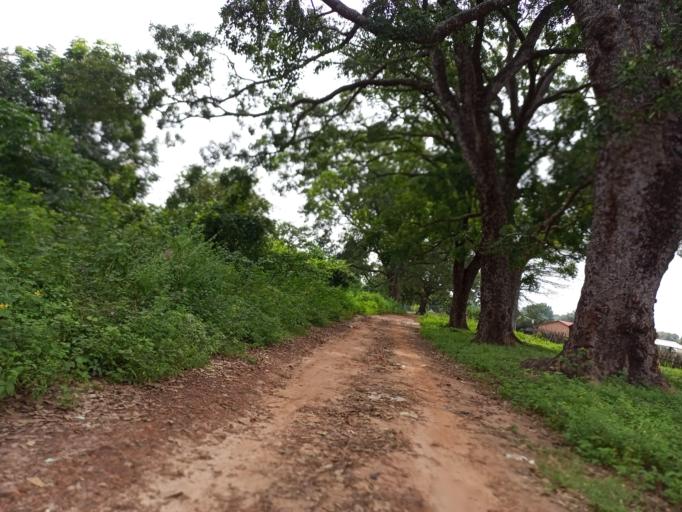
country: GW
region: Oio
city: Farim
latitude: 12.4352
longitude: -15.4199
